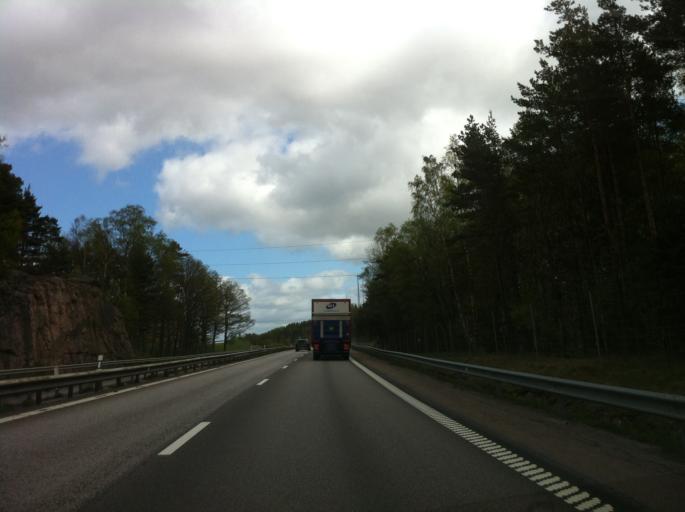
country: SE
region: Vaestra Goetaland
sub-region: Alingsas Kommun
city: Alingsas
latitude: 57.9091
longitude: 12.5049
